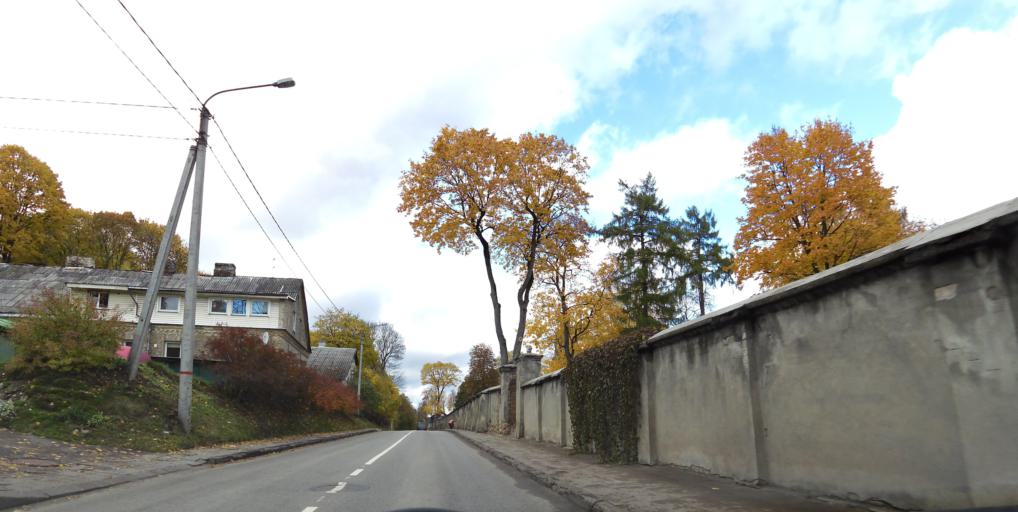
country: LT
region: Vilnius County
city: Rasos
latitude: 54.6680
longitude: 25.3035
